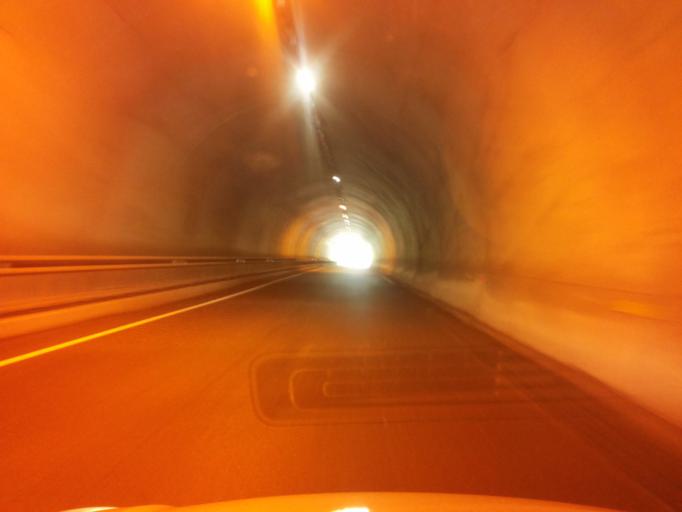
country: IT
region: Piedmont
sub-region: Provincia di Biella
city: Camandona
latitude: 45.6640
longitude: 8.1017
